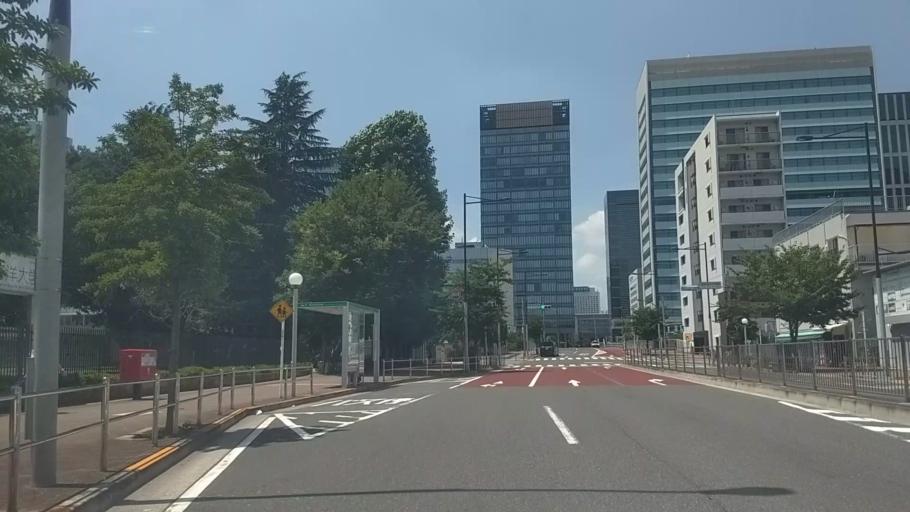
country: JP
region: Tokyo
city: Tokyo
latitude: 35.6289
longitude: 139.7477
